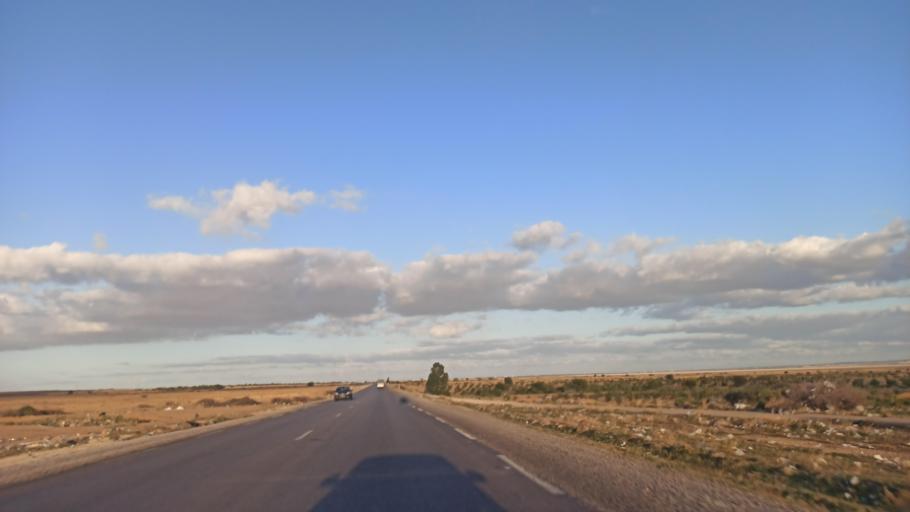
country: TN
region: Al Qayrawan
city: Sbikha
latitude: 35.8898
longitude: 10.2445
